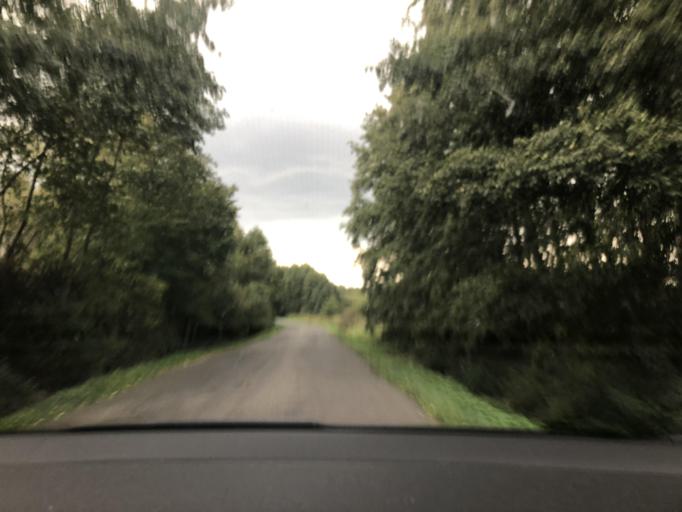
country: CZ
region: Central Bohemia
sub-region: Okres Kolin
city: Tynec nad Labem
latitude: 50.0516
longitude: 15.3806
